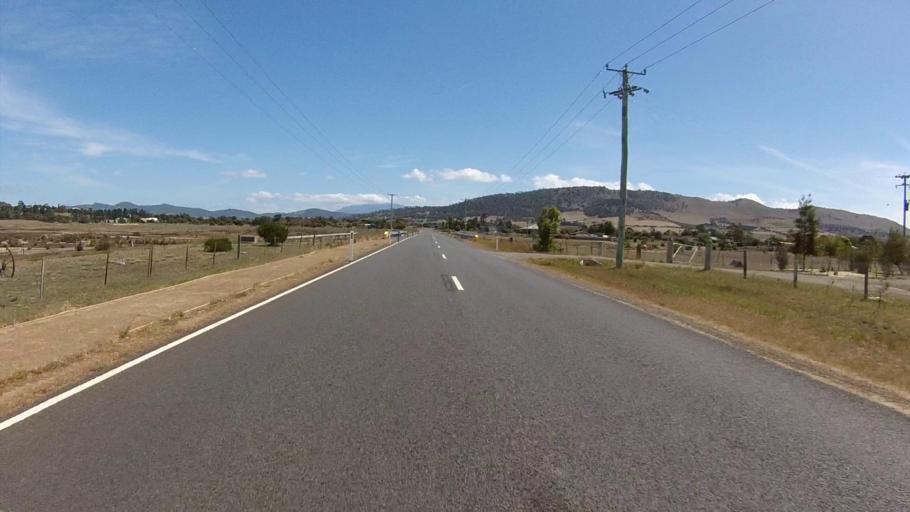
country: AU
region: Tasmania
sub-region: Sorell
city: Sorell
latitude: -42.7767
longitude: 147.5297
